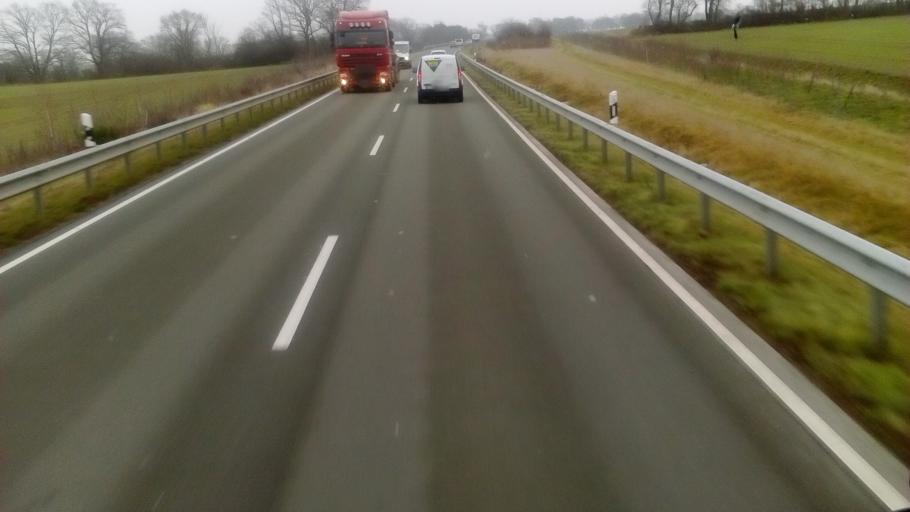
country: DE
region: Brandenburg
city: Pritzwalk
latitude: 53.1491
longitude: 12.1123
